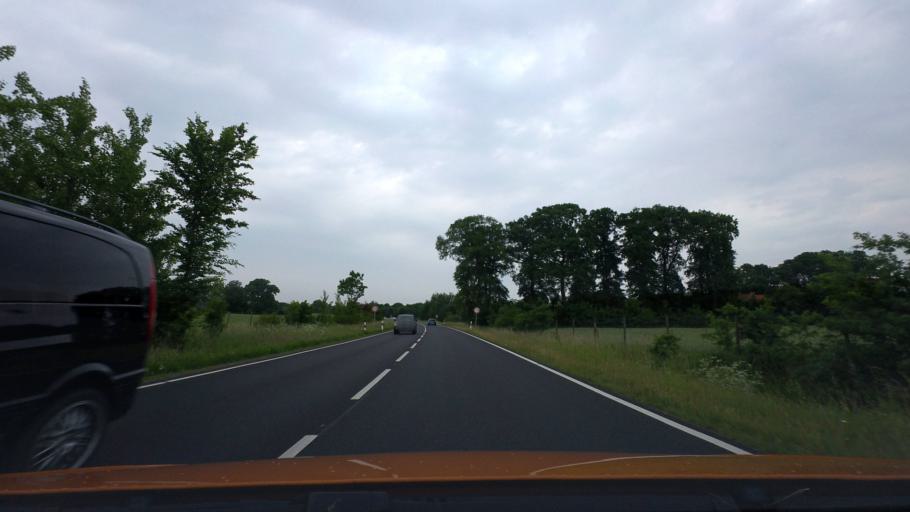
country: DE
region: Lower Saxony
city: Wietzen
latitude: 52.6744
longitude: 9.1062
